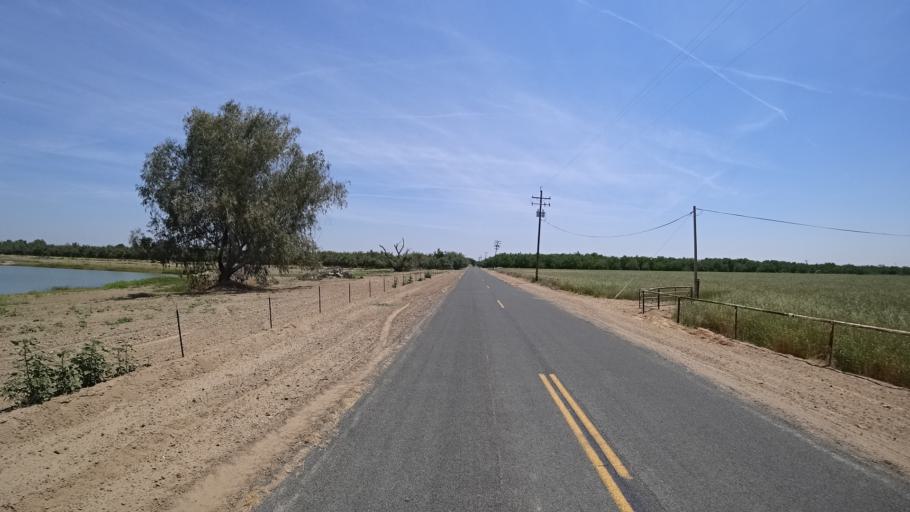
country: US
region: California
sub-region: Fresno County
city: Riverdale
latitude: 36.3948
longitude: -119.8139
